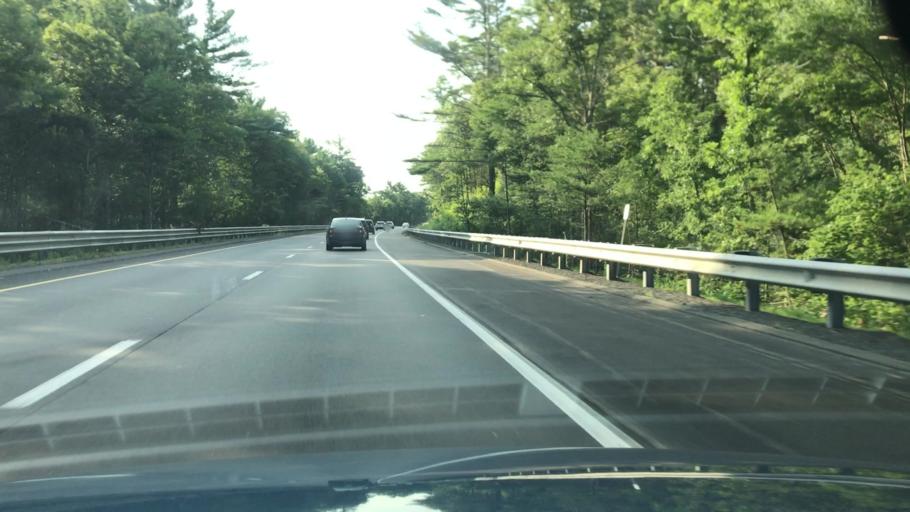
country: US
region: Massachusetts
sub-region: Plymouth County
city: Plymouth
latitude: 41.9264
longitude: -70.6324
